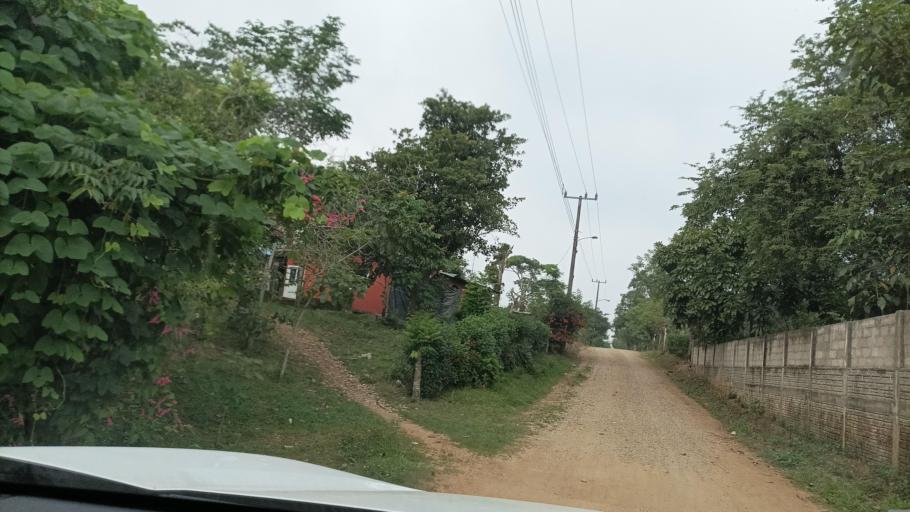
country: MX
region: Veracruz
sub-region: Uxpanapa
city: Poblado 10
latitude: 17.5520
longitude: -94.2246
